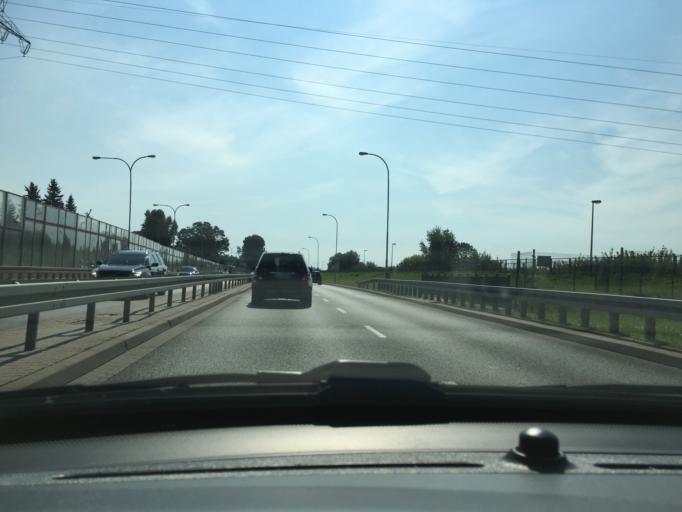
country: PL
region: Masovian Voivodeship
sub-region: Warszawa
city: Wilanow
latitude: 52.2023
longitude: 21.1154
